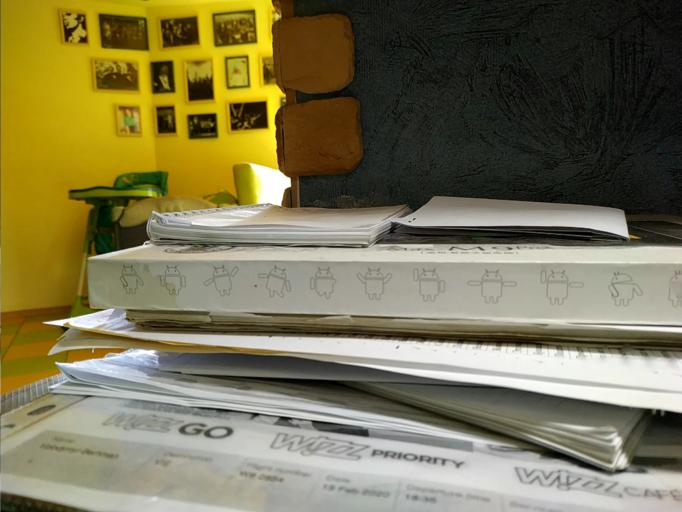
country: RU
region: Pskov
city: Plyussa
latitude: 58.5717
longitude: 29.4542
